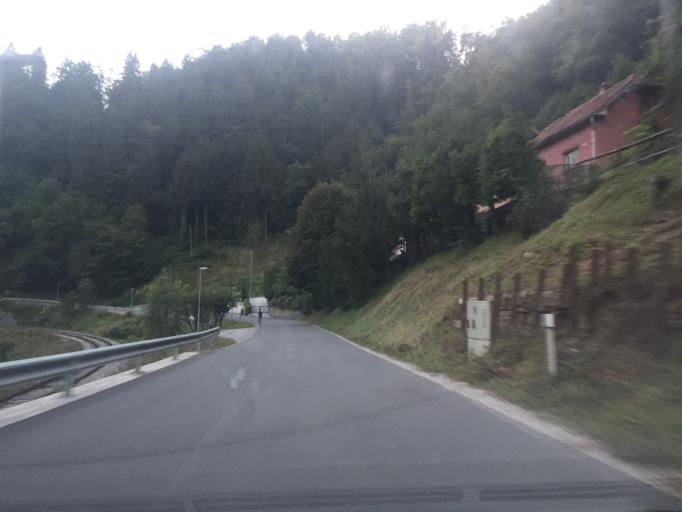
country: SI
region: Sostanj
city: Topolsica
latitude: 46.3804
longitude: 15.0256
